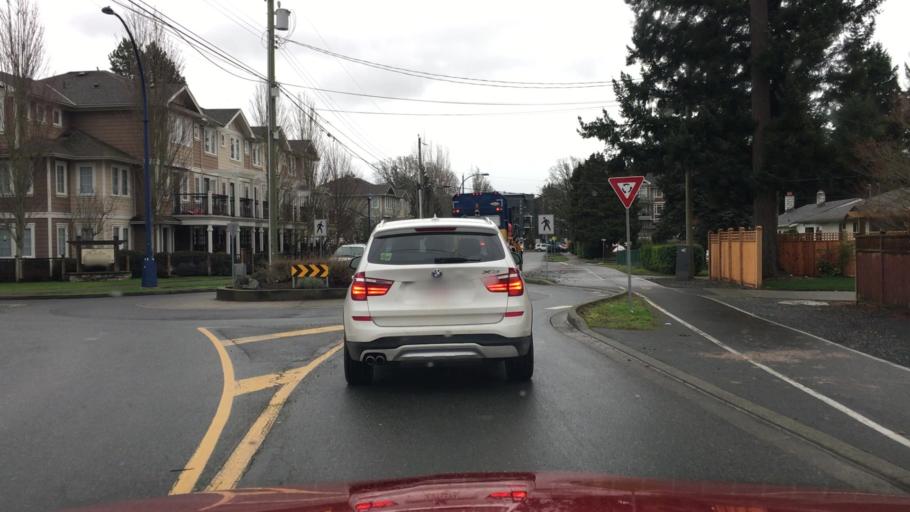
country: CA
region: British Columbia
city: Langford
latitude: 48.4534
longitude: -123.5012
